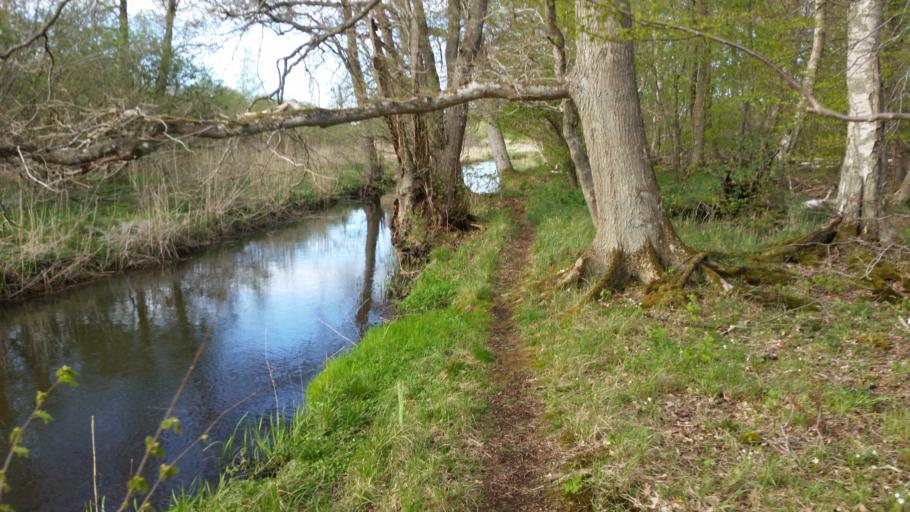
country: DK
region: Capital Region
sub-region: Gribskov Kommune
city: Gilleleje
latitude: 56.0697
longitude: 12.3634
